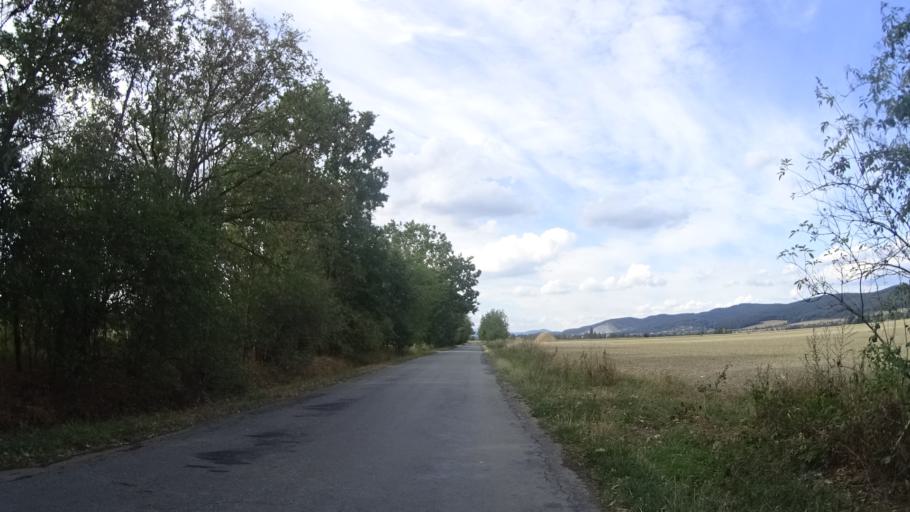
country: CZ
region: Olomoucky
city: Dubicko
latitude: 49.8131
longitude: 16.9429
